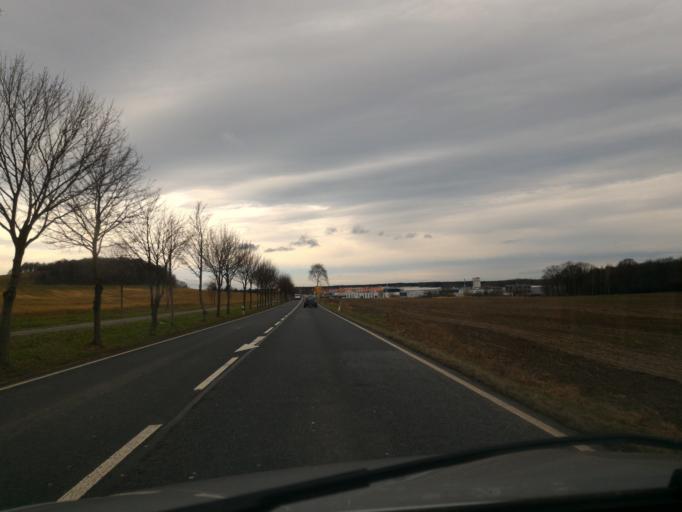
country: DE
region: Saxony
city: Radeberg
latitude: 51.0632
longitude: 13.9056
